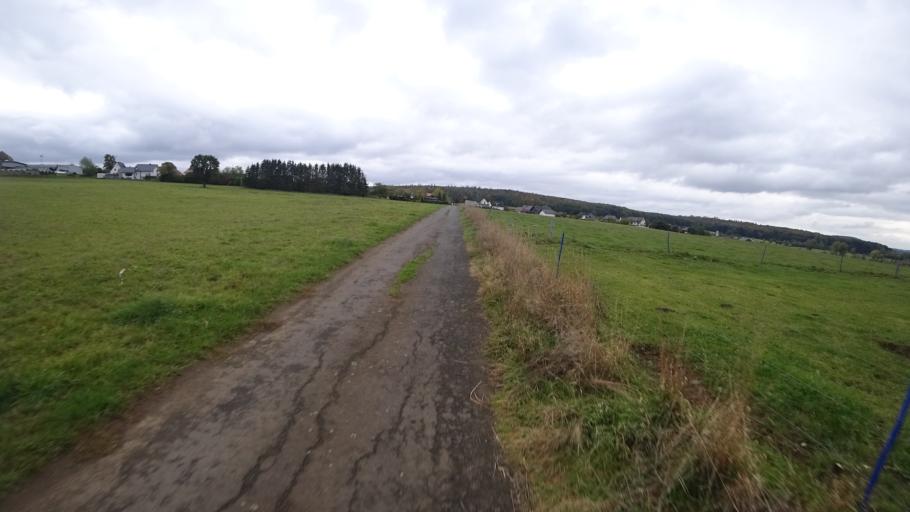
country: DE
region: Rheinland-Pfalz
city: Maxsain
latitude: 50.5484
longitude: 7.7809
